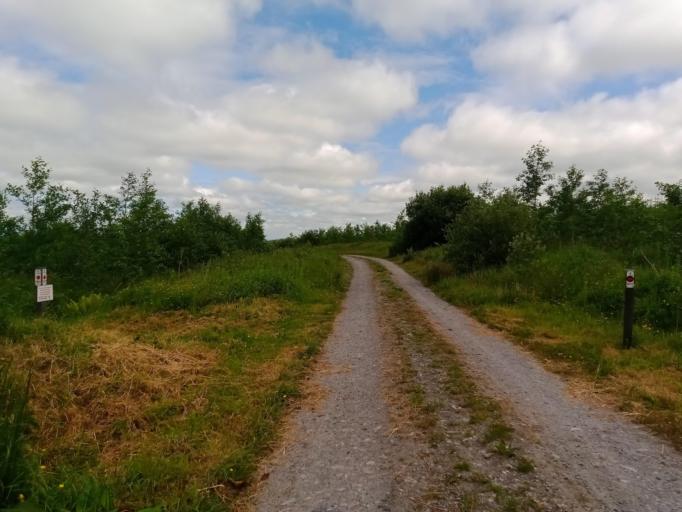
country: IE
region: Leinster
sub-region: Kilkenny
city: Ballyragget
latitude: 52.7927
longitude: -7.4449
